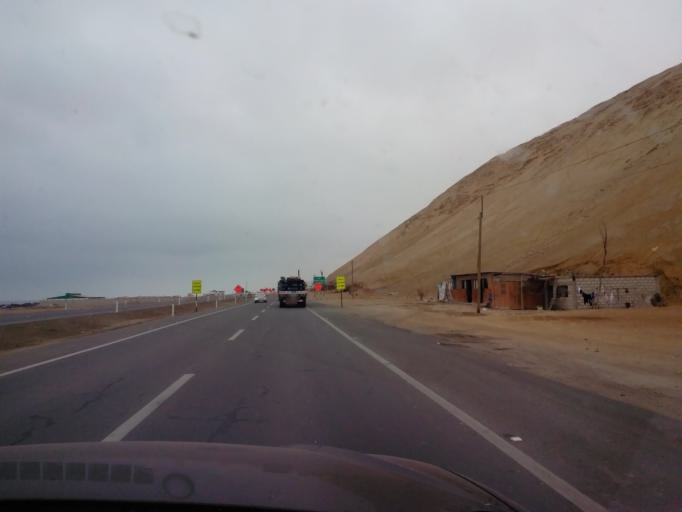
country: PE
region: Ica
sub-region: Provincia de Chincha
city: San Pedro
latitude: -13.3283
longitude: -76.2399
